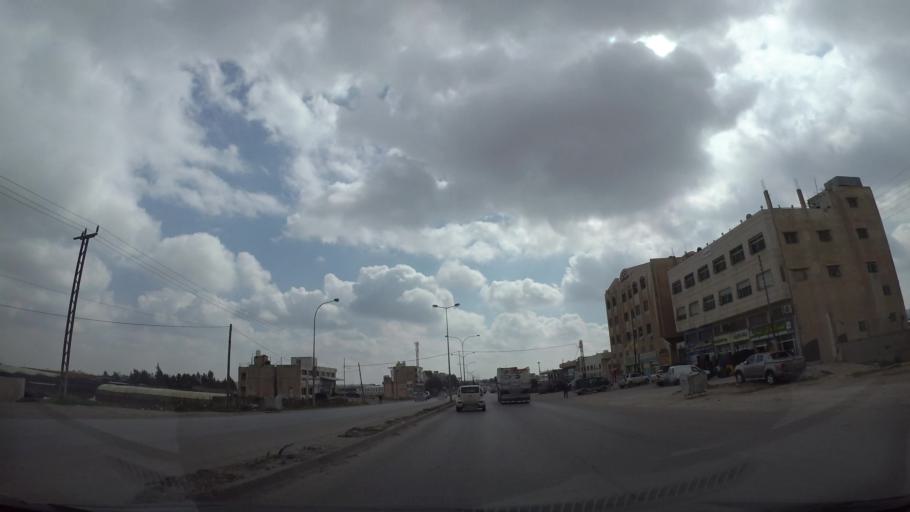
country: JO
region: Amman
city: Jawa
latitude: 31.8254
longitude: 35.9113
